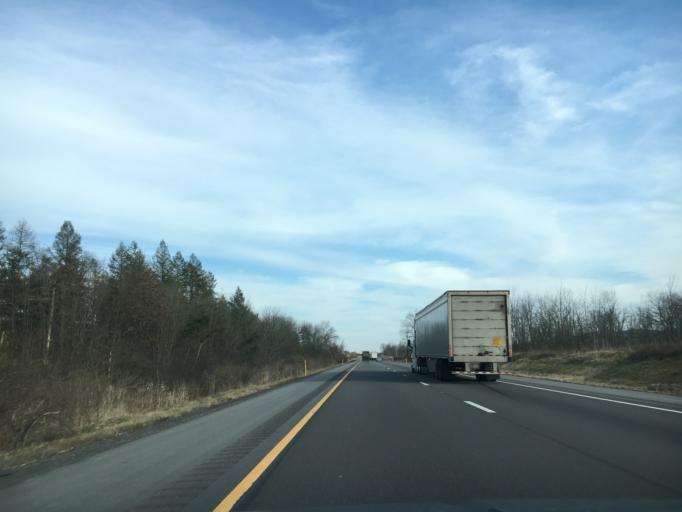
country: US
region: Pennsylvania
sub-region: Montour County
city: Danville
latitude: 40.9990
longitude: -76.6323
